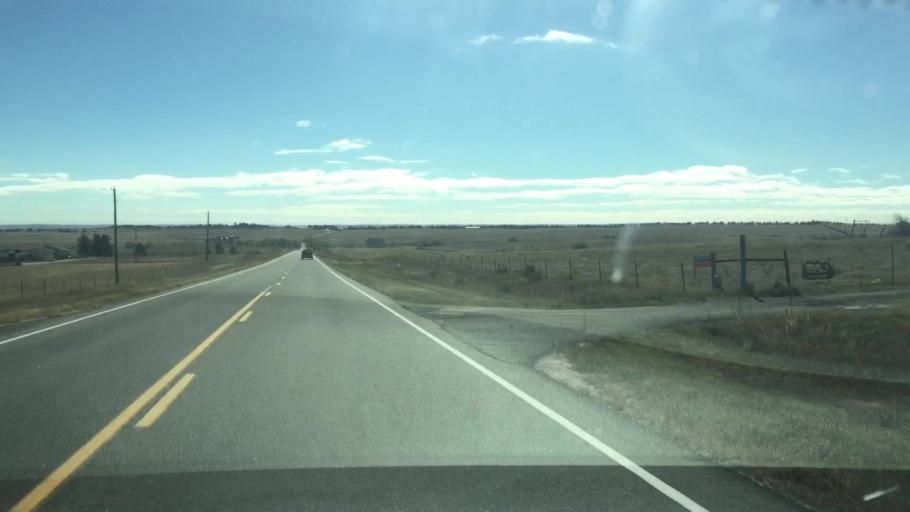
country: US
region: Colorado
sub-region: Elbert County
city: Kiowa
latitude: 39.3282
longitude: -104.4027
